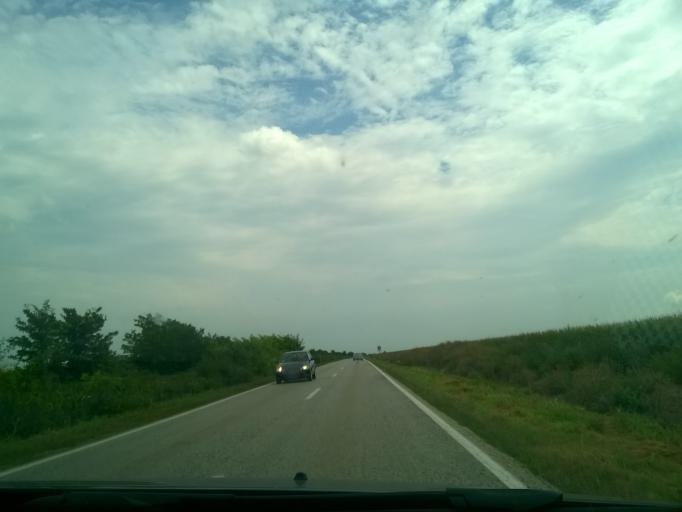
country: RS
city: Banatski Despotovac
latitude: 45.3881
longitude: 20.6082
